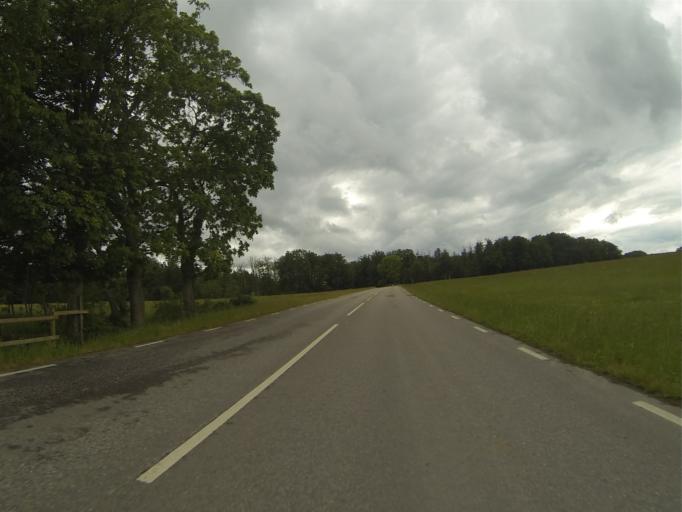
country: SE
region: Skane
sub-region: Lunds Kommun
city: Veberod
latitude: 55.6961
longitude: 13.4221
